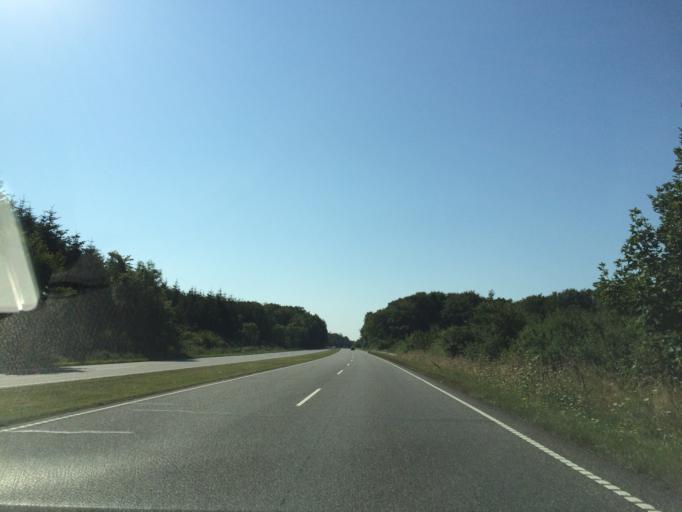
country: DK
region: South Denmark
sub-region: Kolding Kommune
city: Kolding
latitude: 55.5246
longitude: 9.4973
